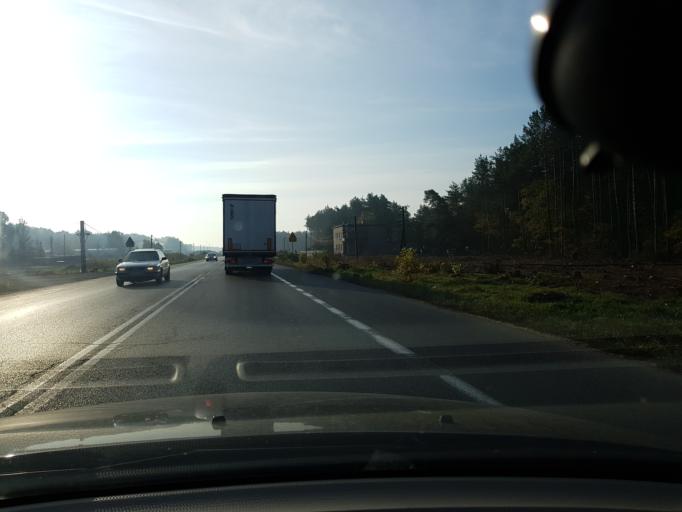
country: PL
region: Masovian Voivodeship
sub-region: Powiat otwocki
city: Otwock
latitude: 52.1602
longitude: 21.3045
